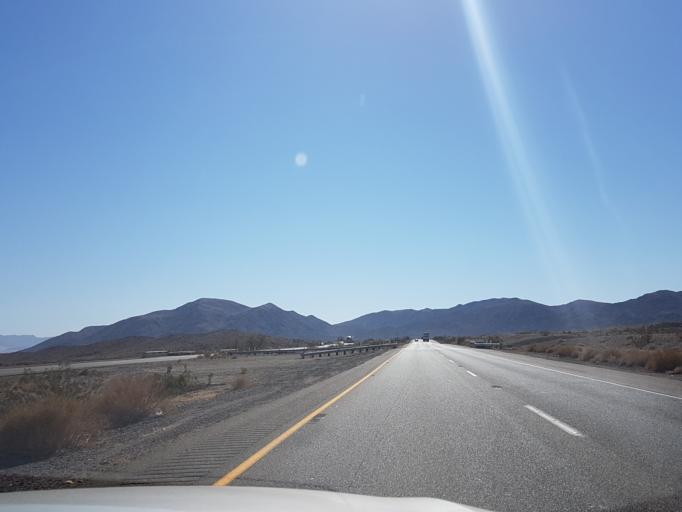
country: US
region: California
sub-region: San Bernardino County
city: Fort Irwin
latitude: 35.2145
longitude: -116.1128
